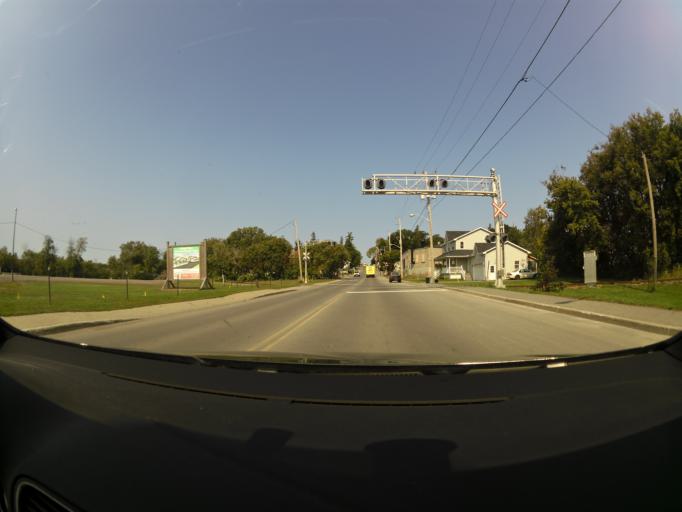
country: CA
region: Ontario
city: Bells Corners
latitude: 45.3435
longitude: -76.0345
